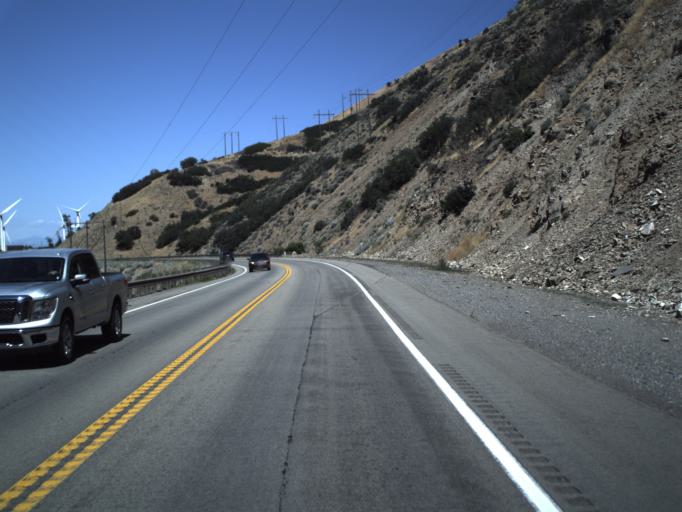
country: US
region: Utah
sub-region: Utah County
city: Mapleton
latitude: 40.0618
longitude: -111.5690
